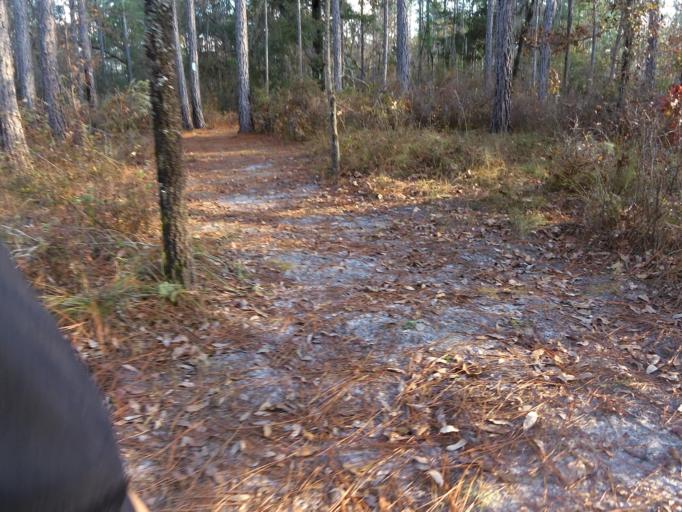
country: US
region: Florida
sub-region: Clay County
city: Middleburg
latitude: 30.1453
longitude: -81.9594
